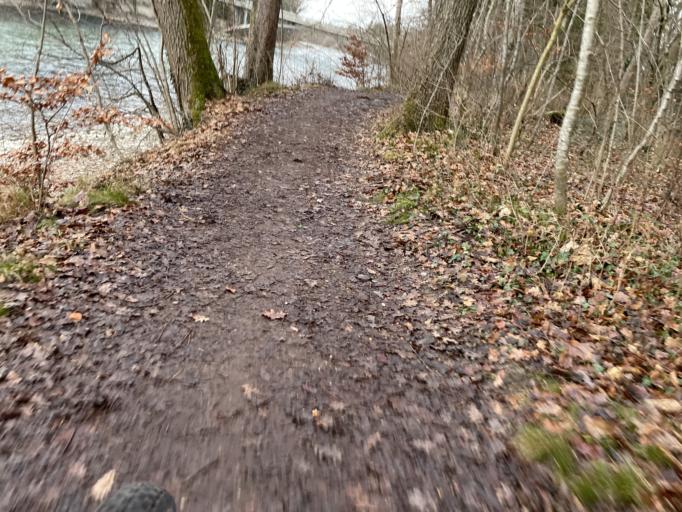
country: CH
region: Bern
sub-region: Thun District
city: Uttigen
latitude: 46.8161
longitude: 7.5716
